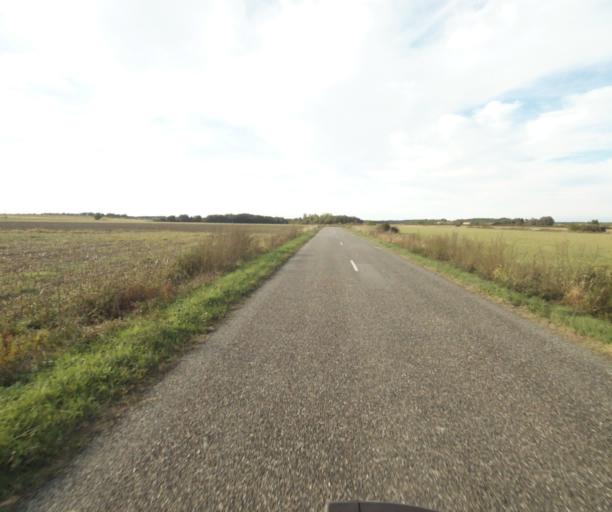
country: FR
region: Midi-Pyrenees
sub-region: Departement du Tarn-et-Garonne
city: Finhan
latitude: 43.9085
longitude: 1.1155
